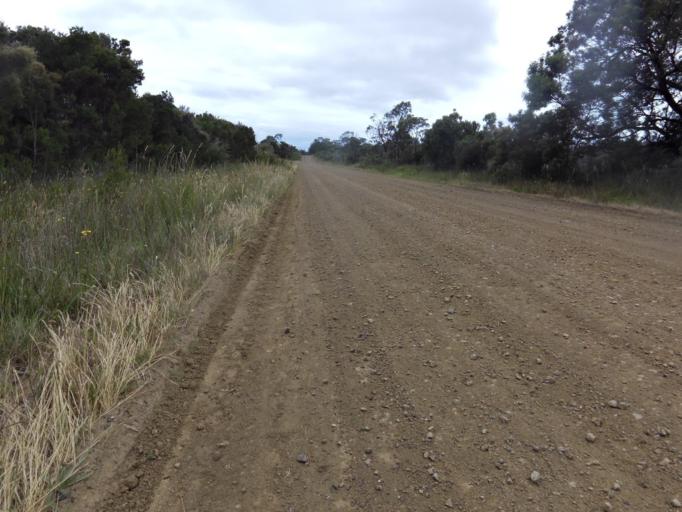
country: AU
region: Victoria
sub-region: Bass Coast
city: Cowes
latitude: -38.3824
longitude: 145.2848
